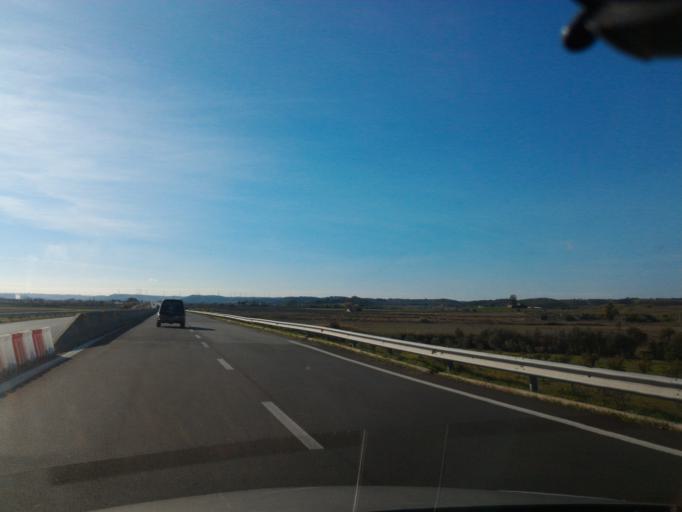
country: IT
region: Calabria
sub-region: Provincia di Crotone
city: Crotone
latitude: 39.1575
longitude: 17.0977
